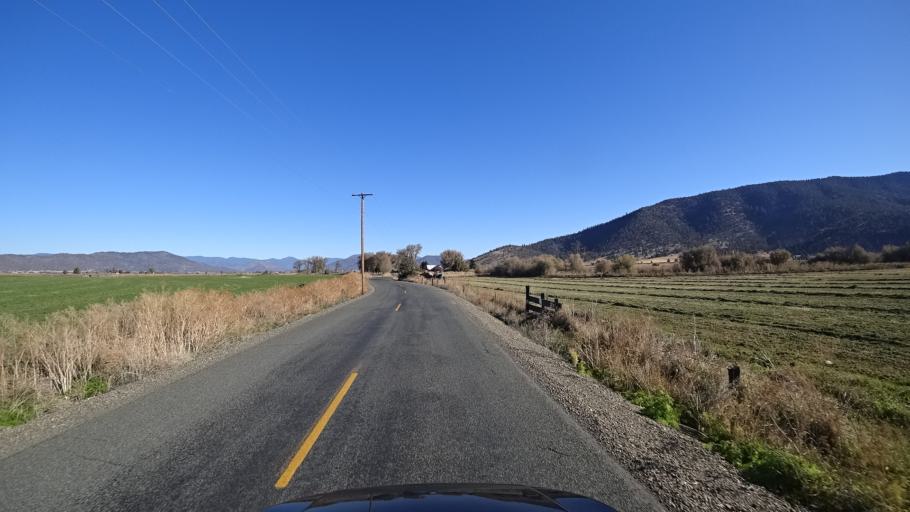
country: US
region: California
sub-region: Siskiyou County
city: Yreka
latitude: 41.5156
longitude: -122.8527
